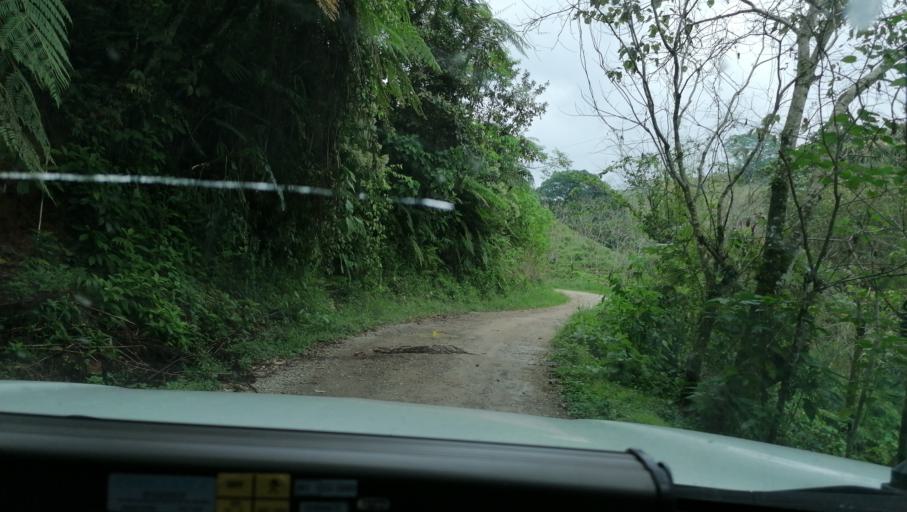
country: MX
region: Chiapas
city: Ocotepec
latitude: 17.3233
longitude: -93.1349
